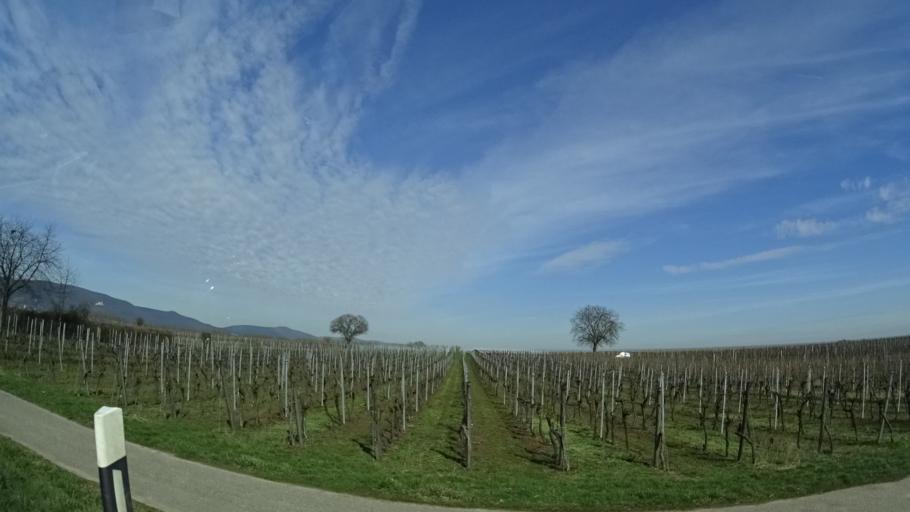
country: DE
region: Rheinland-Pfalz
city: Venningen
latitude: 49.2845
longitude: 8.1638
